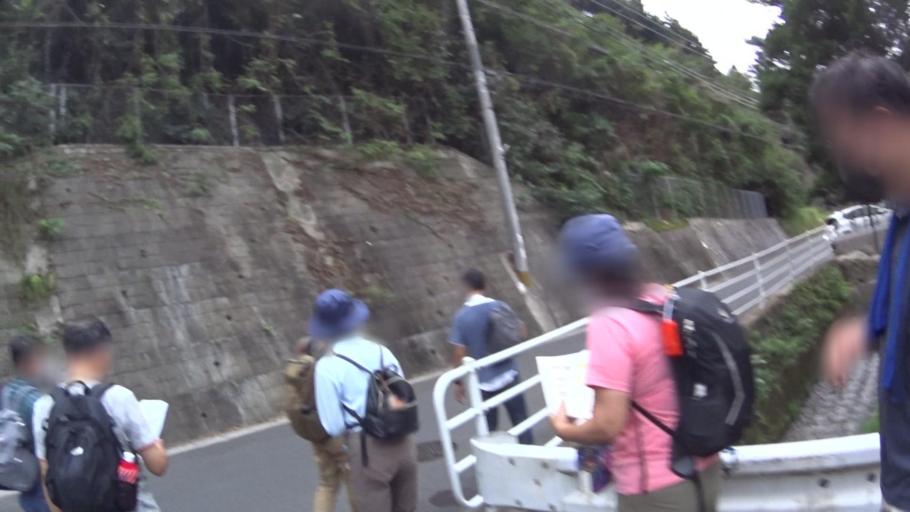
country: JP
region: Osaka
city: Kaizuka
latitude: 34.4586
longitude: 135.2912
